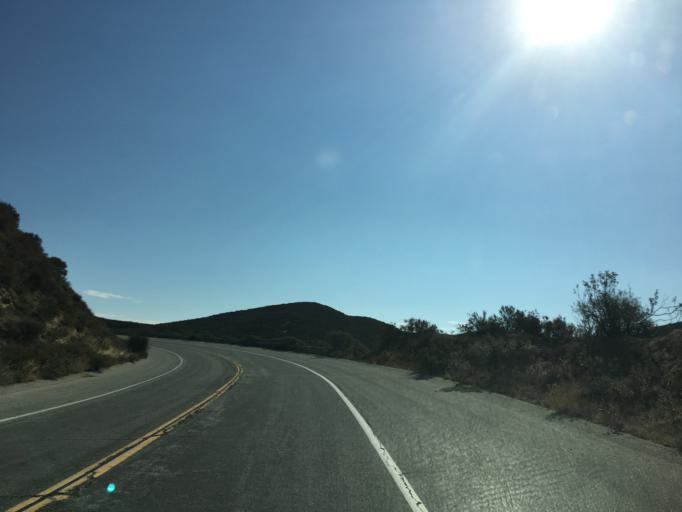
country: US
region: California
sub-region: Los Angeles County
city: Castaic
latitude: 34.5727
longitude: -118.6744
